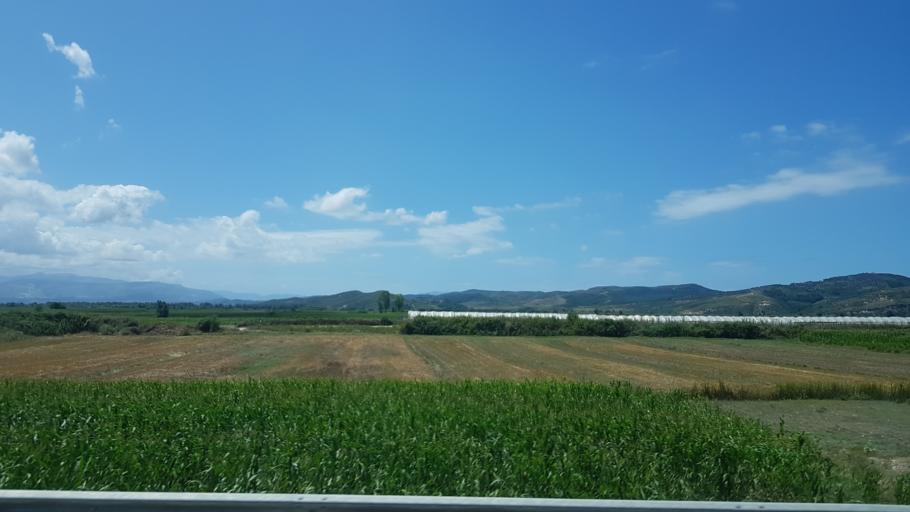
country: AL
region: Fier
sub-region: Rrethi i Fierit
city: Cakran
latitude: 40.5994
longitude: 19.5638
